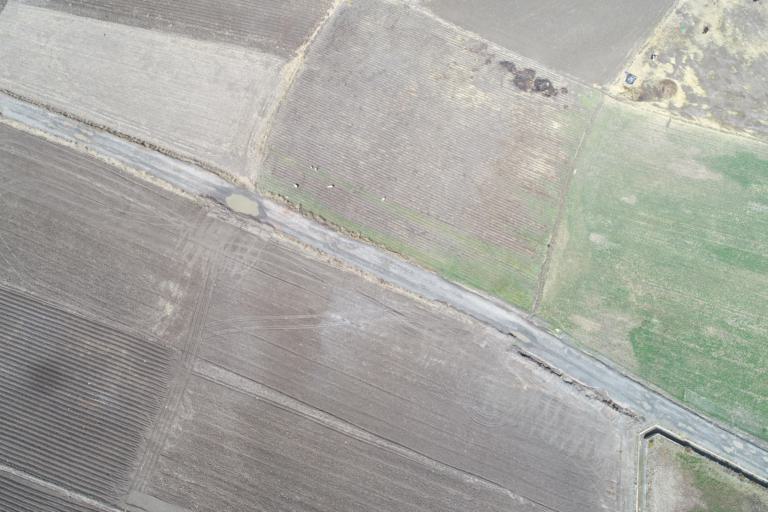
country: BO
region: La Paz
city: Achacachi
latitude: -16.0358
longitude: -68.6836
